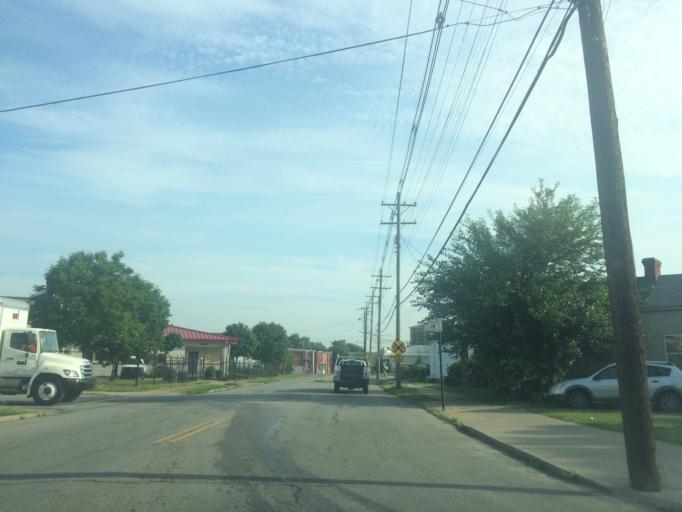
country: US
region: Kentucky
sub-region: Jefferson County
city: Audubon Park
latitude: 38.2284
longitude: -85.7419
